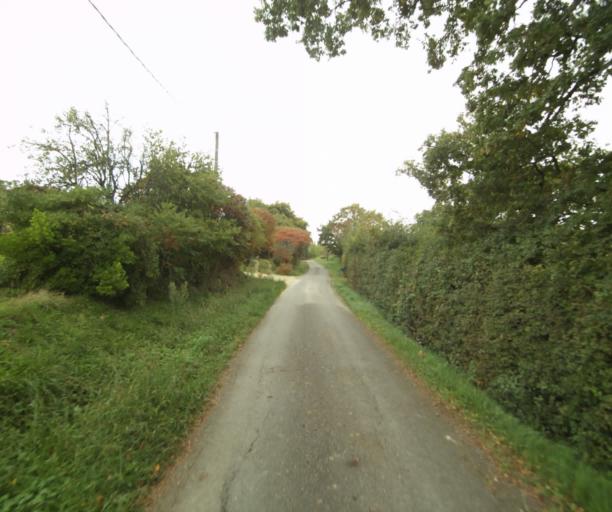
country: FR
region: Midi-Pyrenees
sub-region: Departement du Gers
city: Eauze
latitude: 43.8997
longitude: 0.0971
